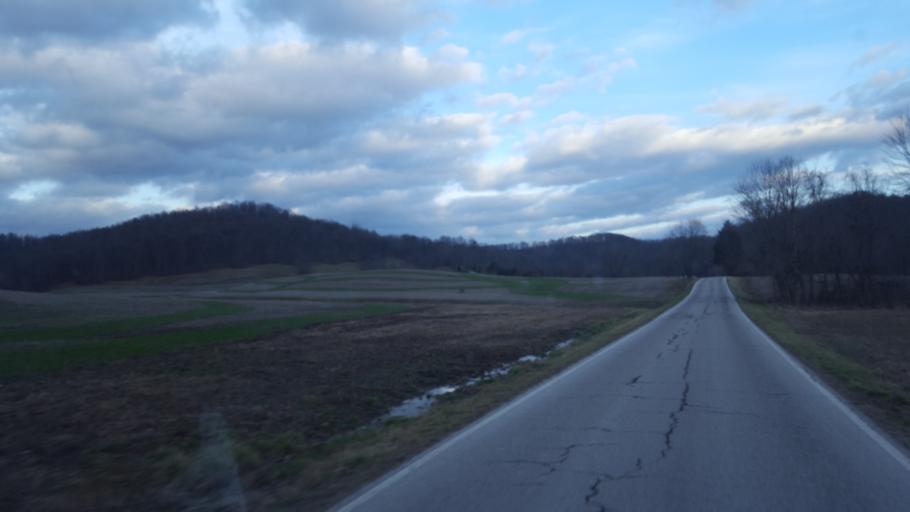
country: US
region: Ohio
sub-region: Adams County
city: Manchester
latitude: 38.5092
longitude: -83.5317
